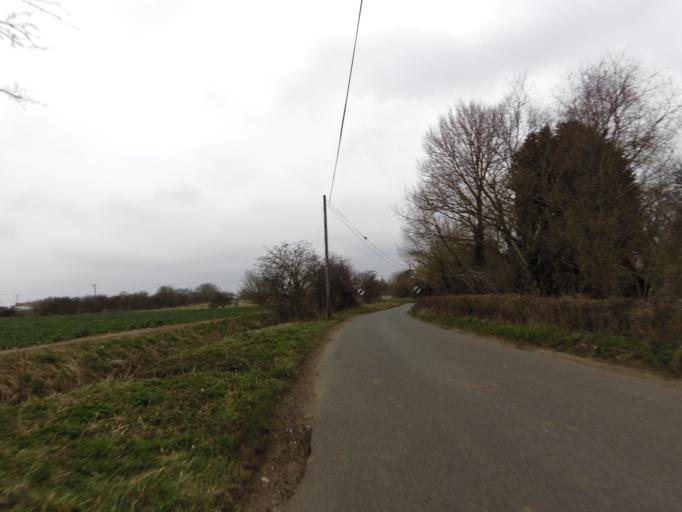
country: GB
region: England
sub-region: Suffolk
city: Framlingham
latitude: 52.2206
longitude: 1.3318
